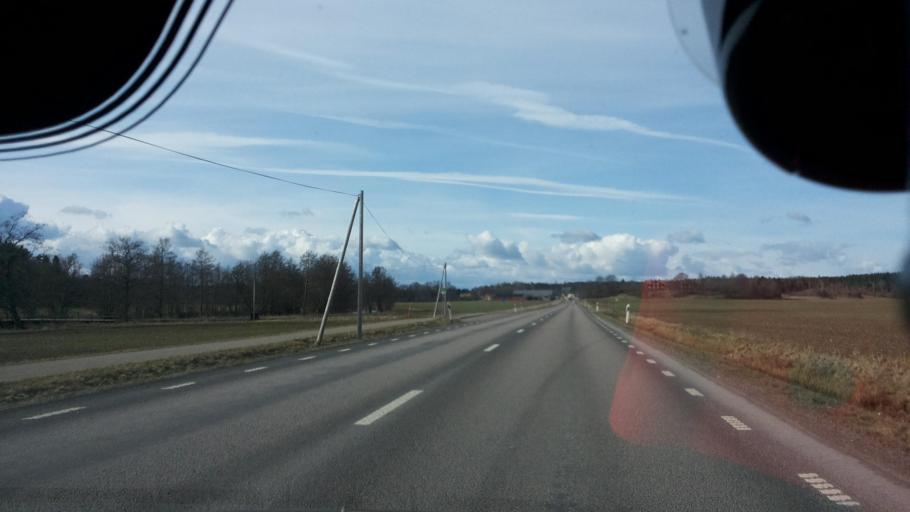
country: SE
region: Soedermanland
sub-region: Trosa Kommun
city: Trosa
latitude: 58.9191
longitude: 17.5427
